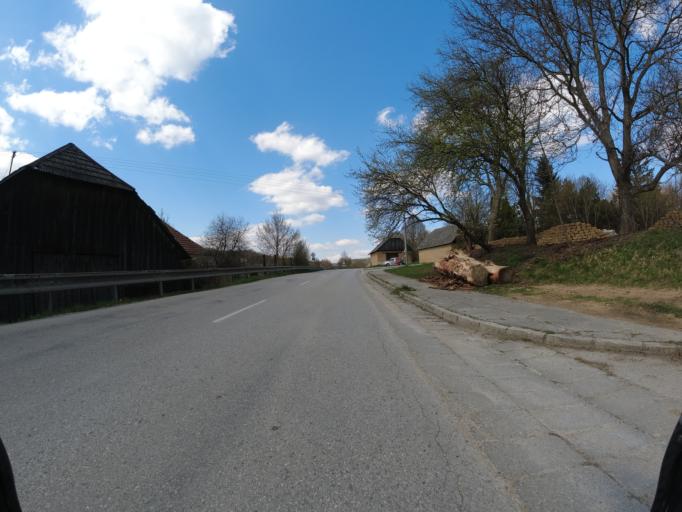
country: SK
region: Nitriansky
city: Stara Tura
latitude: 48.7426
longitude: 17.7222
